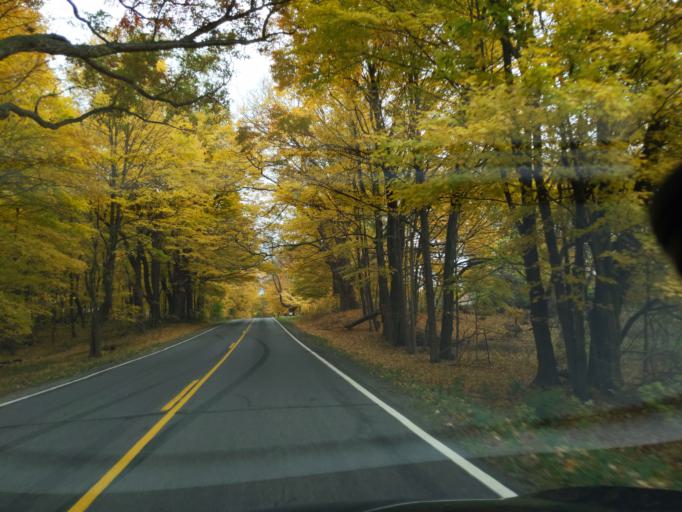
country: US
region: Michigan
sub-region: Jackson County
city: Spring Arbor
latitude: 42.3398
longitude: -84.6005
